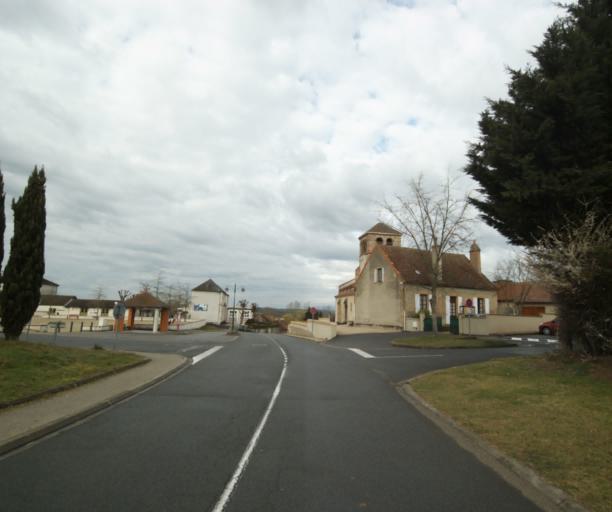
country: FR
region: Auvergne
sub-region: Departement de l'Allier
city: Toulon-sur-Allier
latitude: 46.5185
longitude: 3.3602
